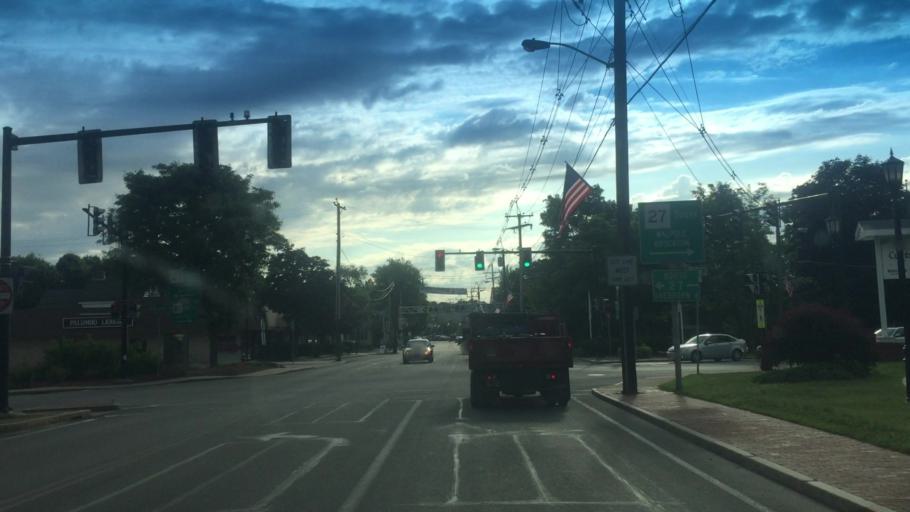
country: US
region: Massachusetts
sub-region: Norfolk County
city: Medfield
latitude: 42.1854
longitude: -71.3093
